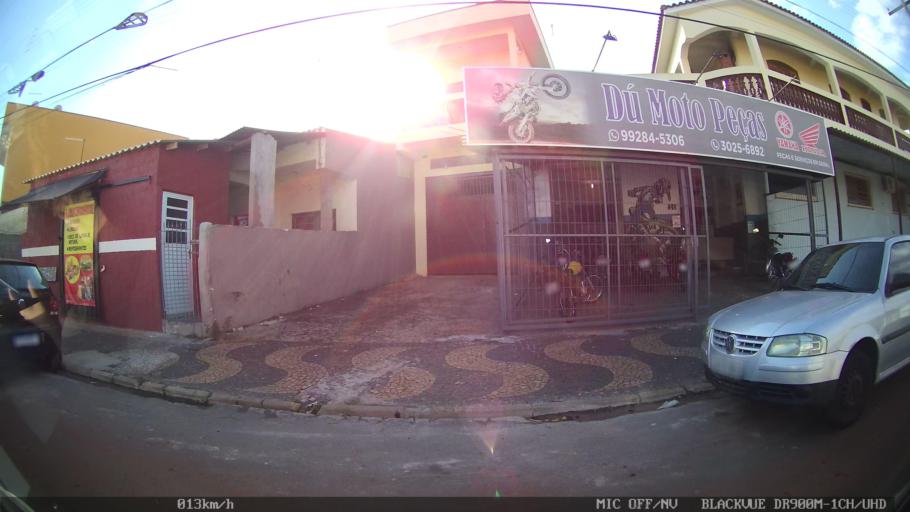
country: BR
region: Sao Paulo
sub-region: Santa Barbara D'Oeste
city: Santa Barbara d'Oeste
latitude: -22.7415
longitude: -47.3760
